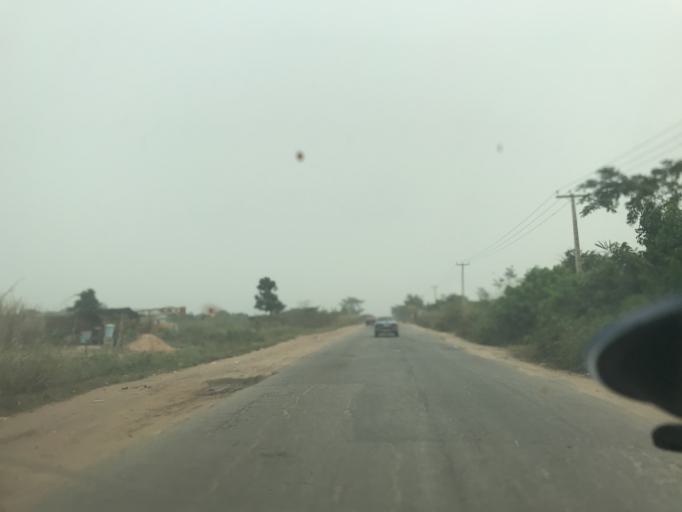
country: NG
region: Ogun
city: Itori
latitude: 6.8891
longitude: 3.1532
